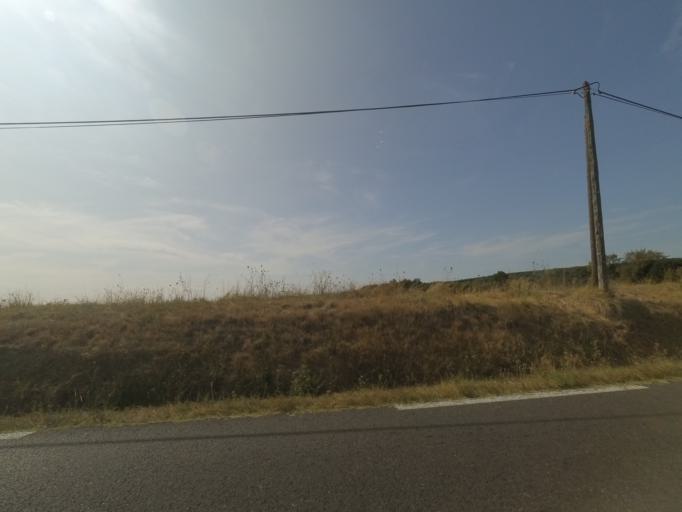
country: FR
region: Languedoc-Roussillon
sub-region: Departement du Gard
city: Villevieille
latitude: 43.8225
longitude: 4.1278
